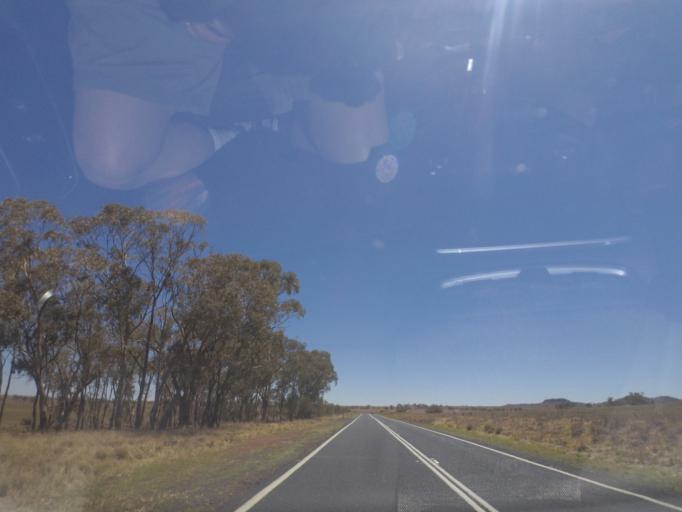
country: AU
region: New South Wales
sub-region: Warrumbungle Shire
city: Coonabarabran
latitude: -31.4459
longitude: 149.1502
